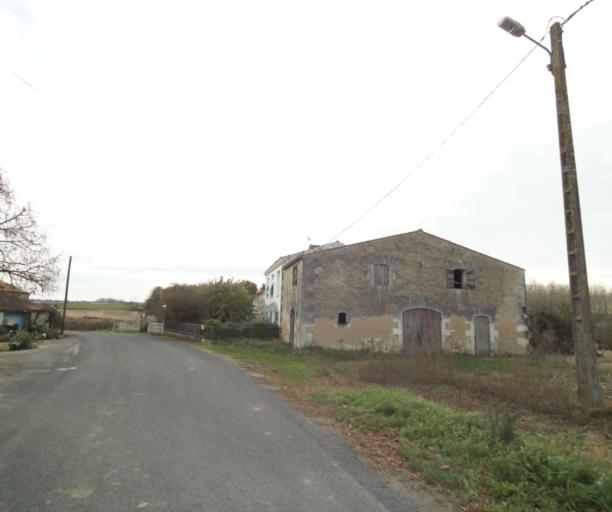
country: FR
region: Poitou-Charentes
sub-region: Departement de la Charente-Maritime
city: Saint-Porchaire
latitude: 45.7936
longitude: -0.8119
